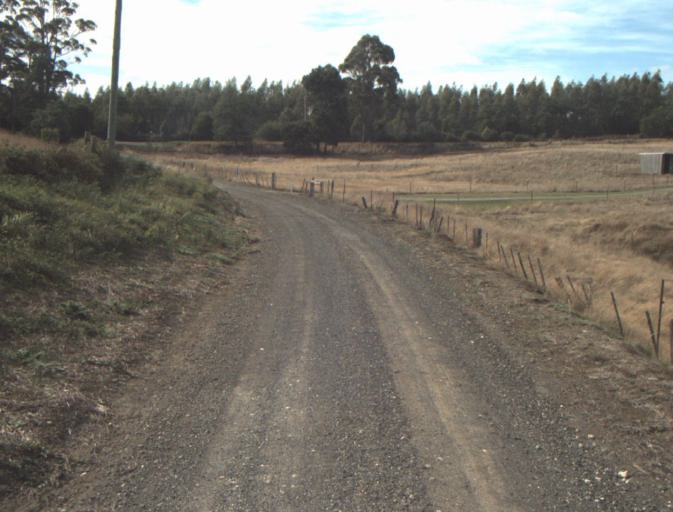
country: AU
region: Tasmania
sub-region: Launceston
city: Mayfield
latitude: -41.1958
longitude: 147.1951
